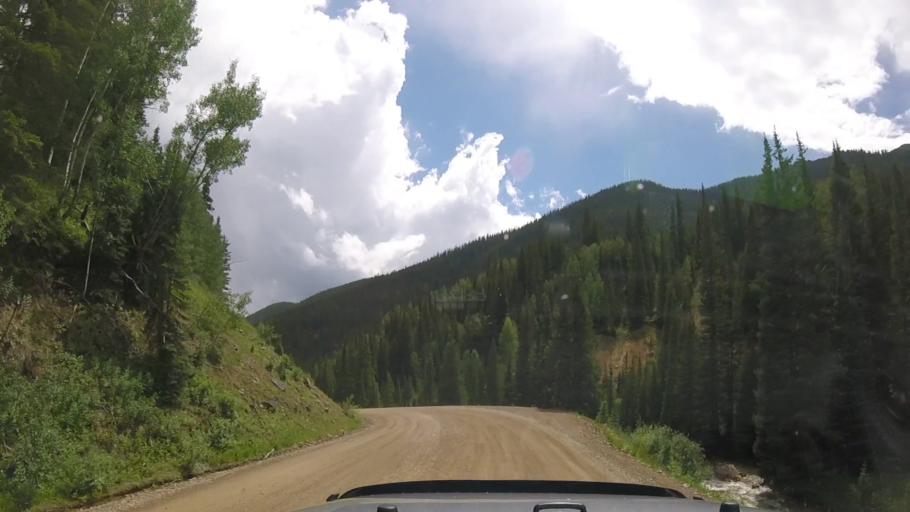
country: US
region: Colorado
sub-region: San Juan County
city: Silverton
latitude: 37.8387
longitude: -107.6787
